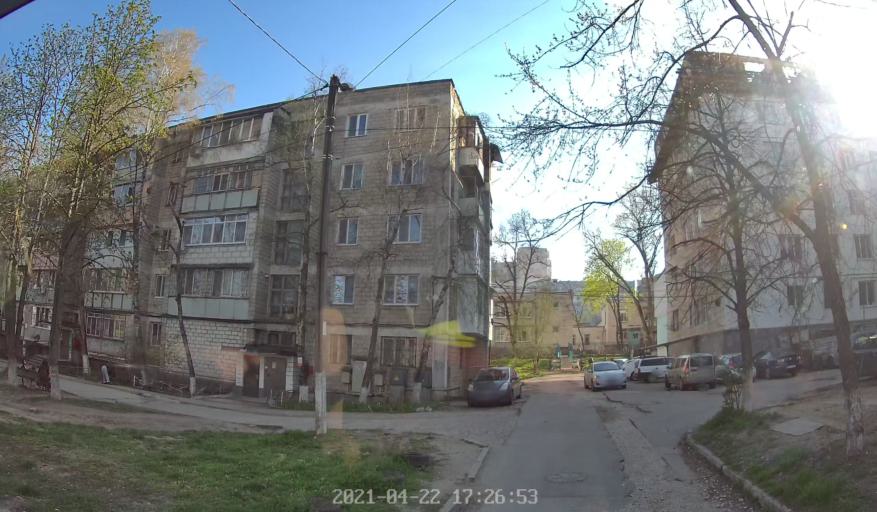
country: MD
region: Chisinau
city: Chisinau
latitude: 47.0353
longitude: 28.8807
